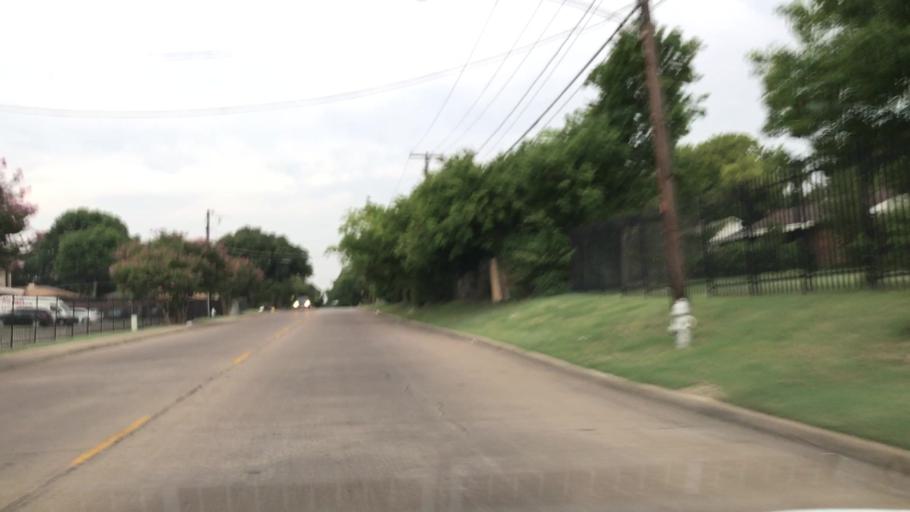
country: US
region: Texas
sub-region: Dallas County
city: Highland Park
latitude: 32.7917
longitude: -96.7124
